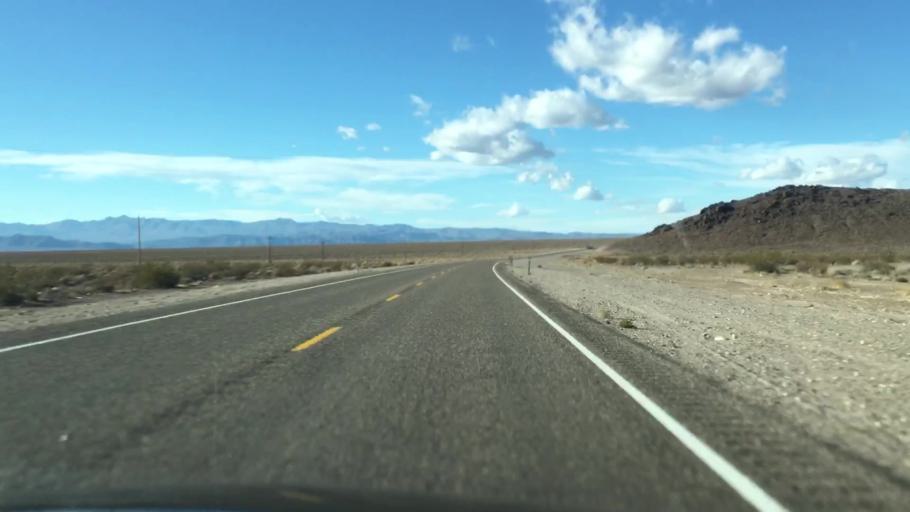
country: US
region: Nevada
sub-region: Nye County
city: Beatty
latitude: 37.1784
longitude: -116.9289
